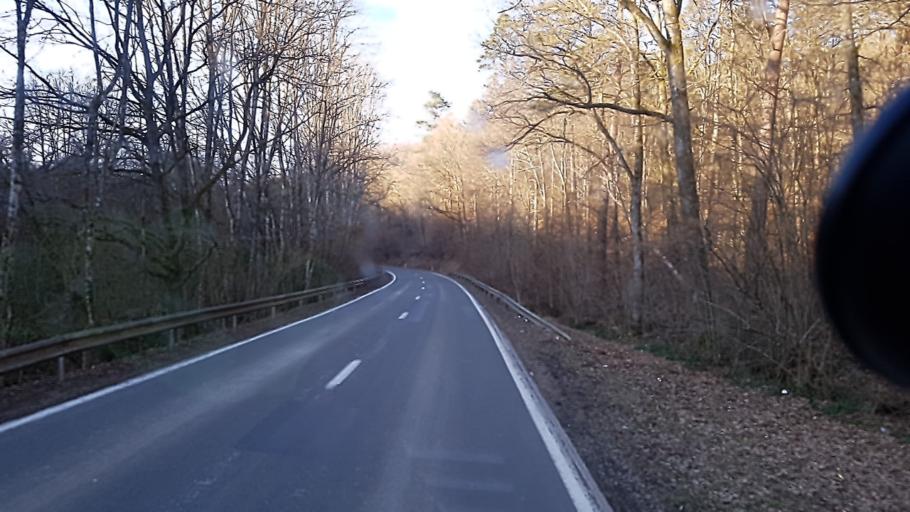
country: BE
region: Wallonia
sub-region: Province du Luxembourg
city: Libin
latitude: 49.9794
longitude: 5.1829
